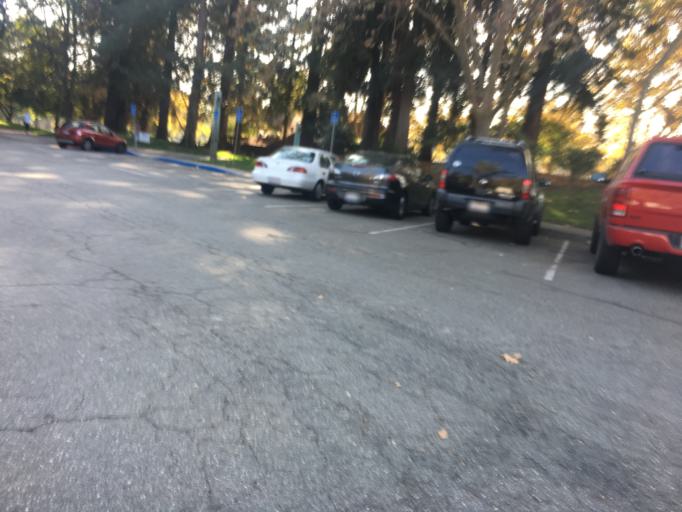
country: US
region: California
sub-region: Santa Clara County
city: Mountain View
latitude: 37.3724
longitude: -122.0827
